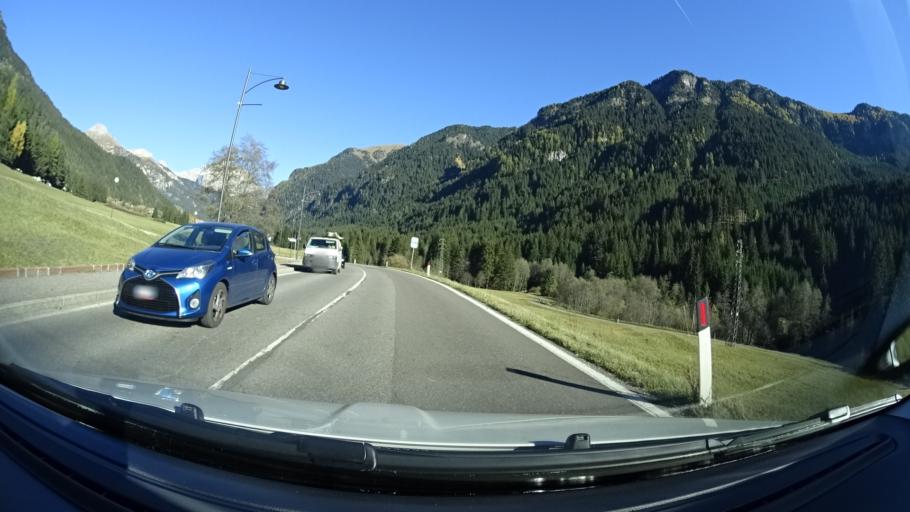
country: IT
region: Trentino-Alto Adige
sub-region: Provincia di Trento
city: Mazzin
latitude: 46.4597
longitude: 11.7058
